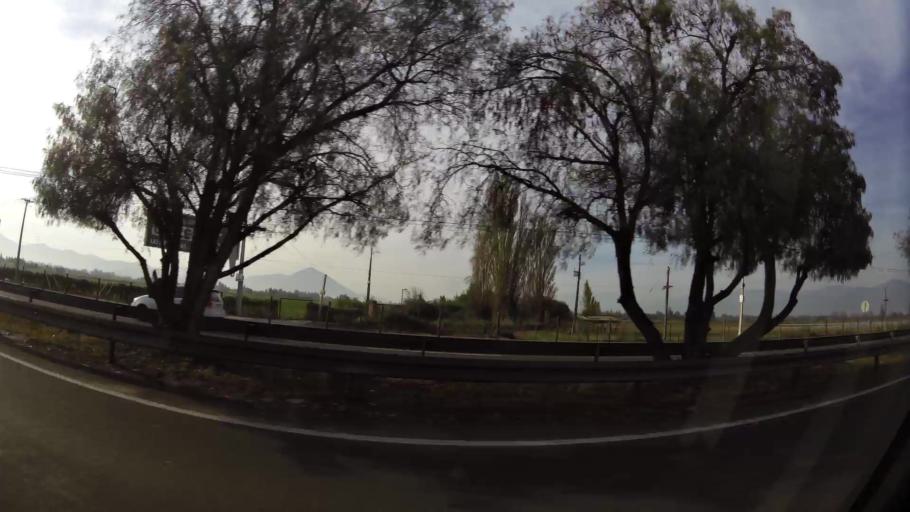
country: CL
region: Santiago Metropolitan
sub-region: Provincia de Talagante
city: Talagante
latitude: -33.6617
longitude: -70.9019
